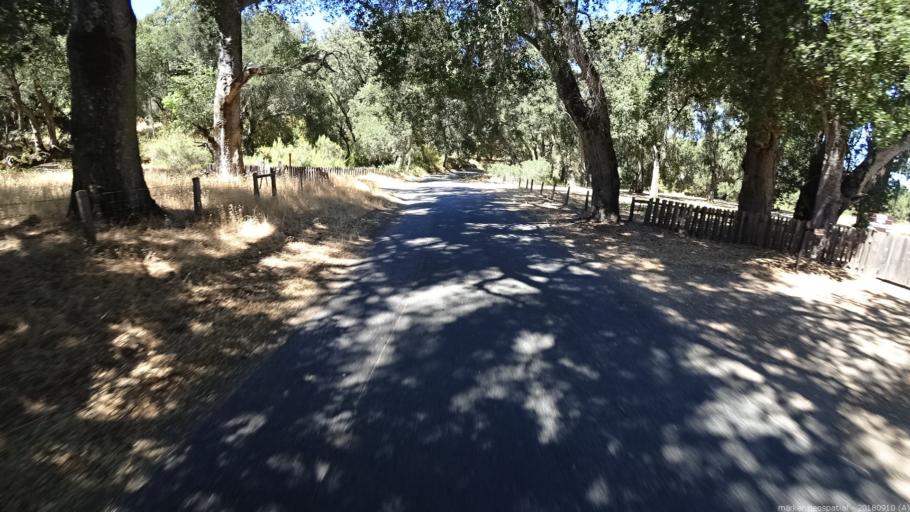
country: US
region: California
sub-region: Monterey County
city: Carmel Valley Village
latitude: 36.4399
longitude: -121.7970
